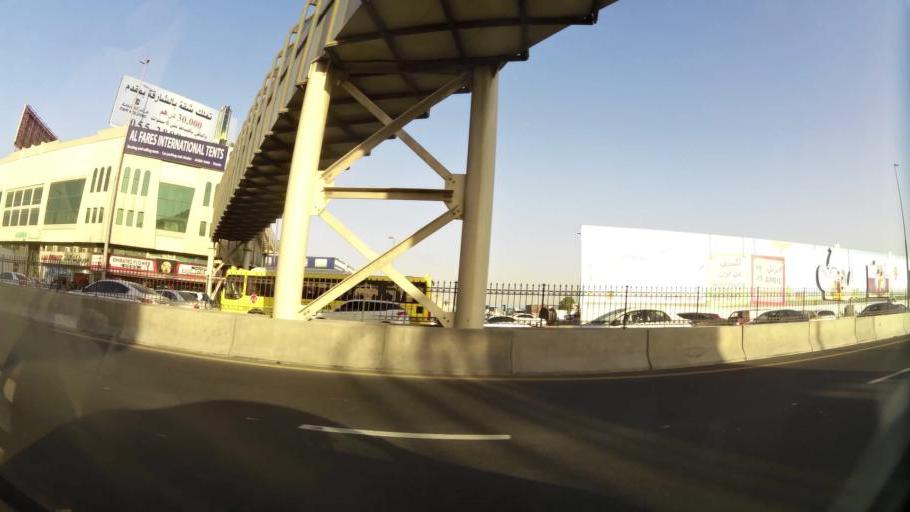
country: AE
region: Ash Shariqah
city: Sharjah
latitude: 25.2934
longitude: 55.4338
